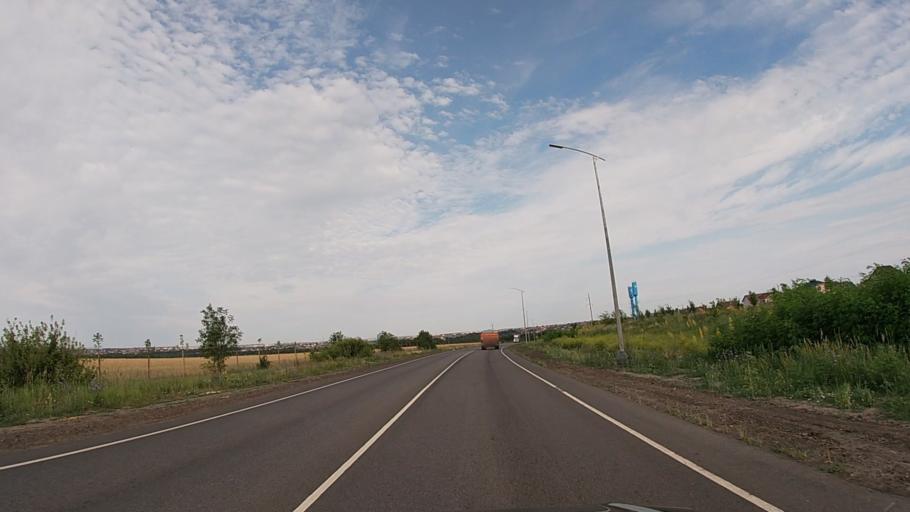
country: RU
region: Belgorod
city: Severnyy
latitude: 50.6654
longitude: 36.5006
